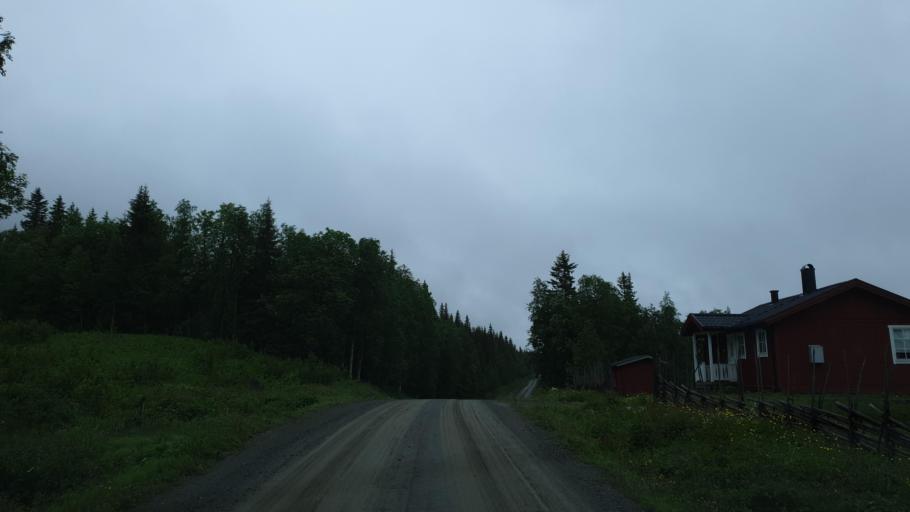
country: SE
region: Vaesterbotten
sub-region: Vilhelmina Kommun
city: Sjoberg
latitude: 65.3433
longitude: 15.8792
